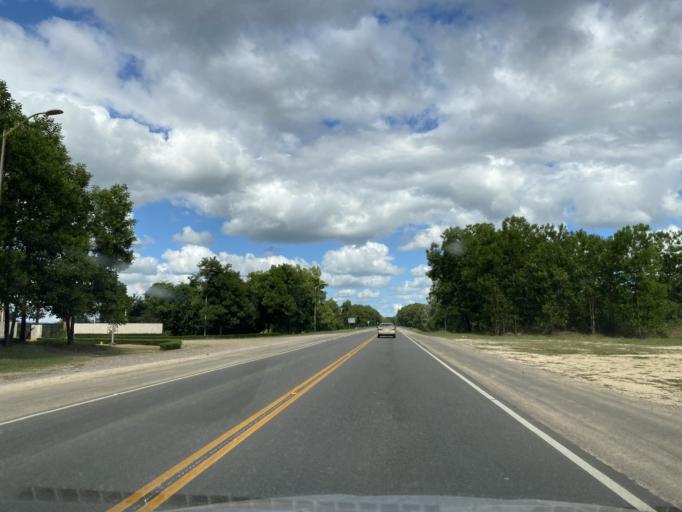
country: DO
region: Santo Domingo
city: Guerra
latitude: 18.6489
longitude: -69.7520
